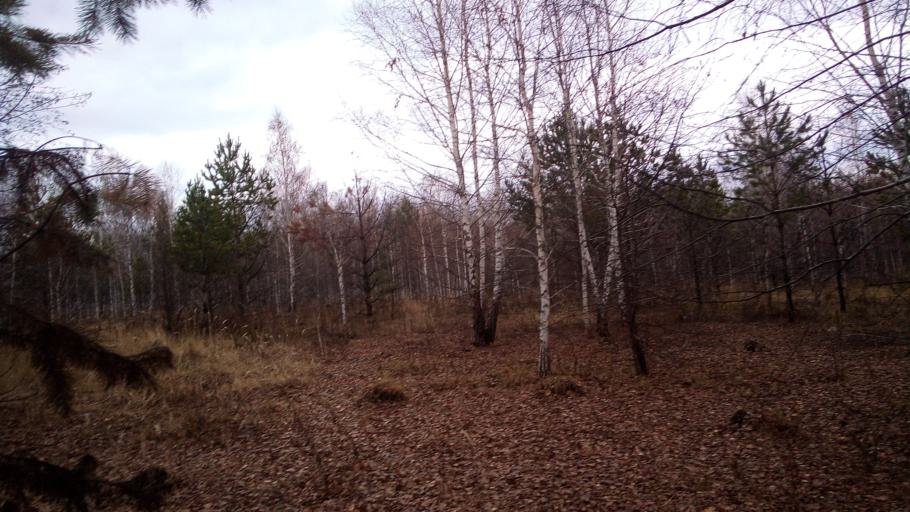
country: RU
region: Chelyabinsk
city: Sargazy
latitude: 55.1241
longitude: 61.2498
